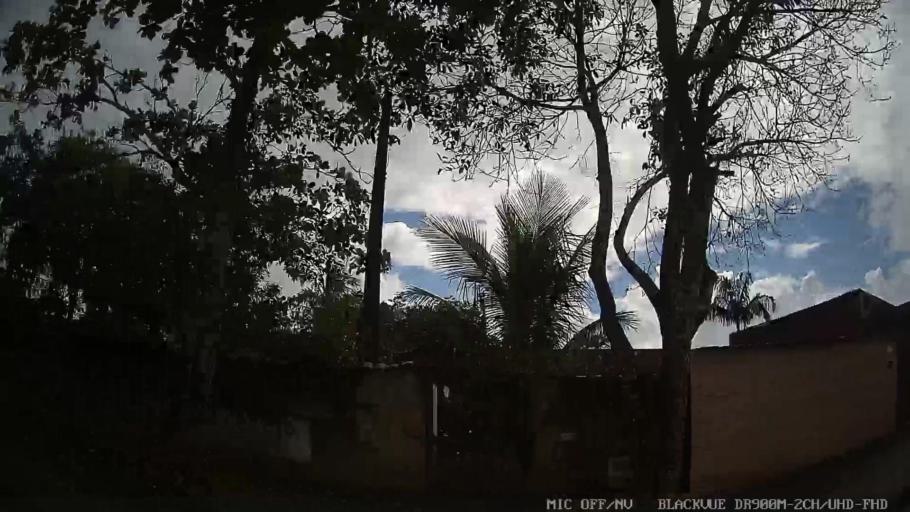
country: BR
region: Sao Paulo
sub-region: Itanhaem
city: Itanhaem
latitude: -24.1590
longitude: -46.7980
